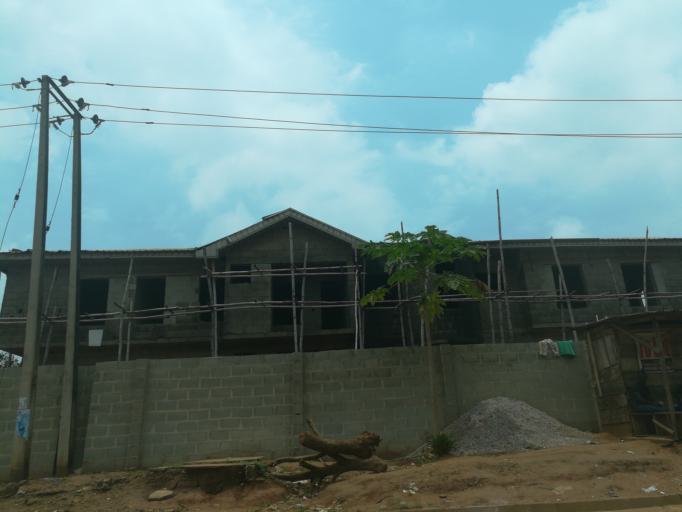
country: NG
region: Lagos
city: Ikorodu
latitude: 6.6266
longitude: 3.5322
